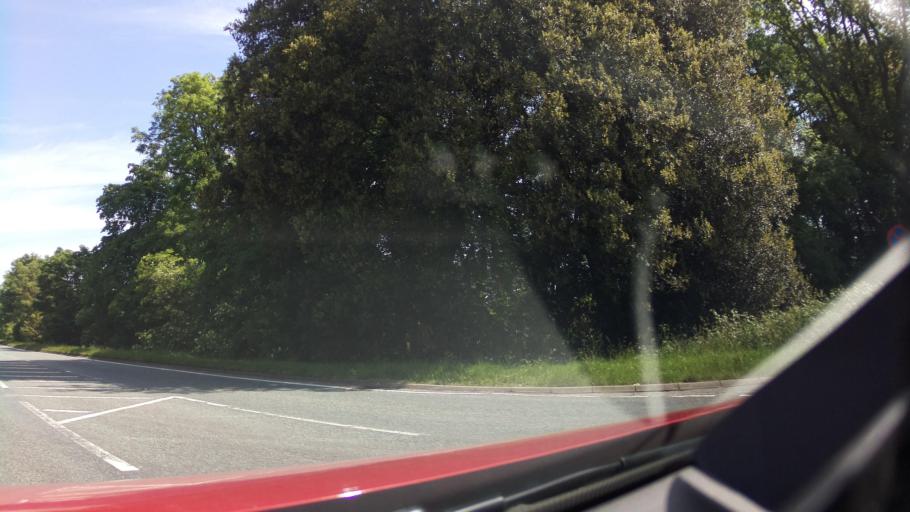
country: GB
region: England
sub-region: Lincolnshire
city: Burton
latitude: 53.3623
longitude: -0.5455
